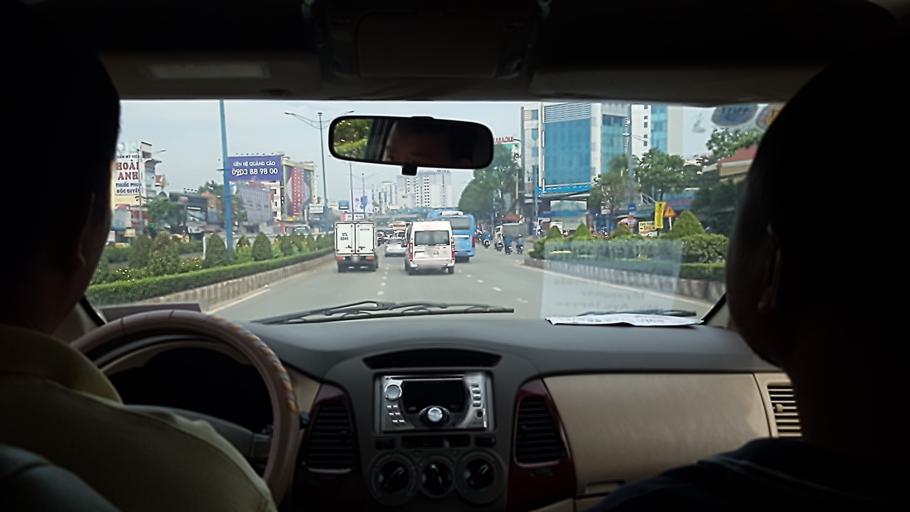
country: VN
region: Ho Chi Minh City
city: Ho Chi Minh City
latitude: 10.8256
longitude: 106.6270
